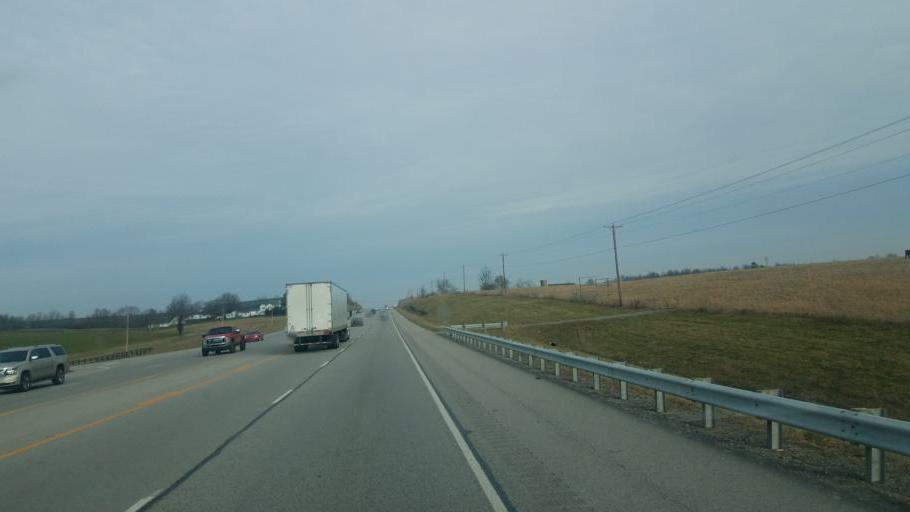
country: US
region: Kentucky
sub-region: Boyle County
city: Junction City
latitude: 37.6048
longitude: -84.7738
